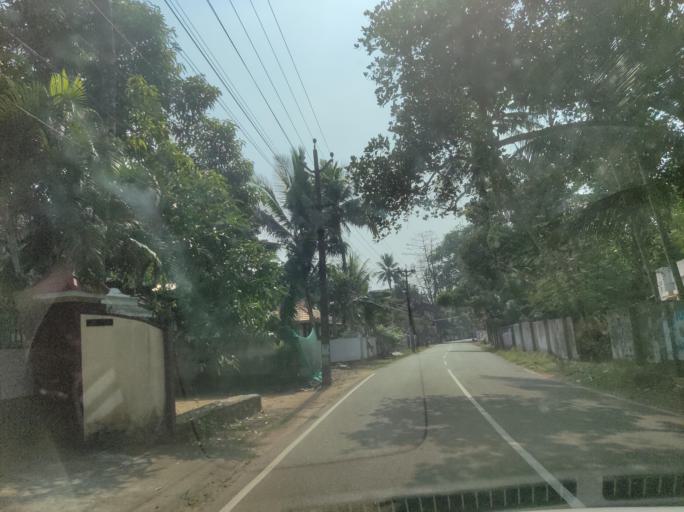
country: IN
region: Kerala
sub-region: Pattanamtitta
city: Tiruvalla
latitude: 9.3456
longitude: 76.5640
